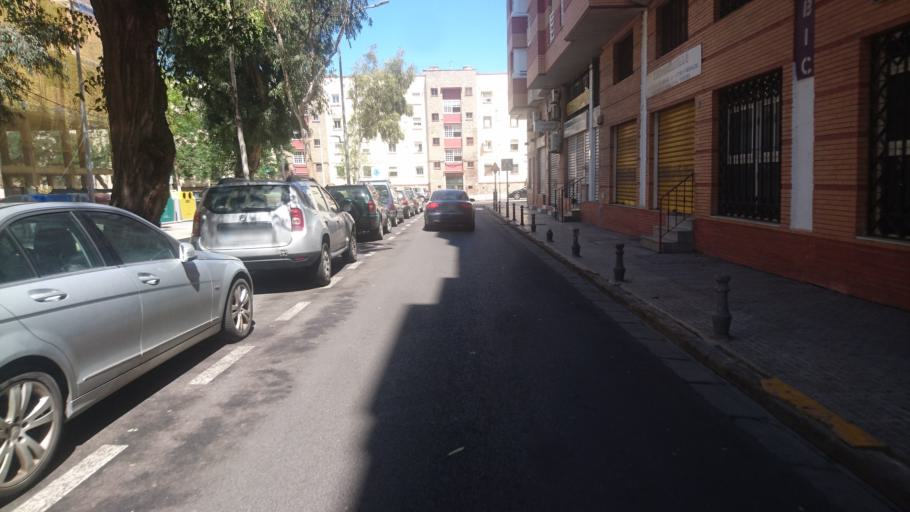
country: ES
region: Melilla
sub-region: Melilla
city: Melilla
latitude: 35.2754
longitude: -2.9393
